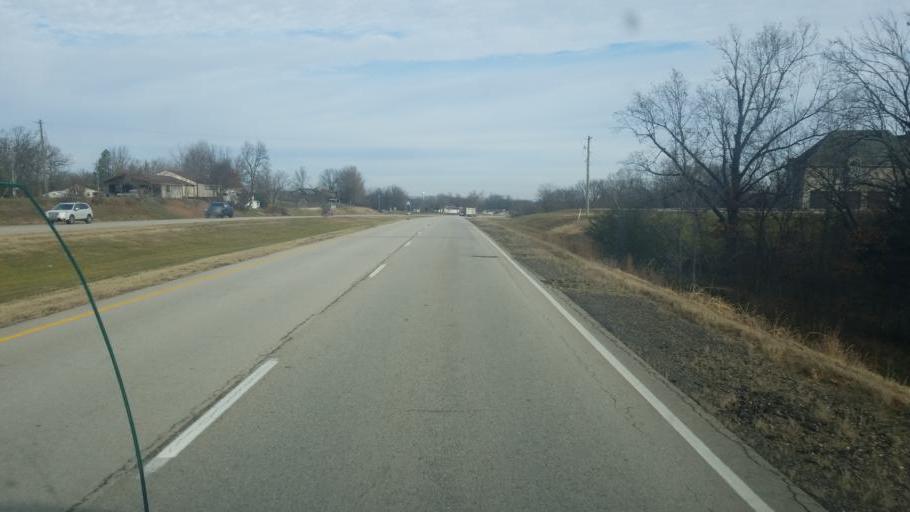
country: US
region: Missouri
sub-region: Stoddard County
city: Bloomfield
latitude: 36.8691
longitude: -89.9295
